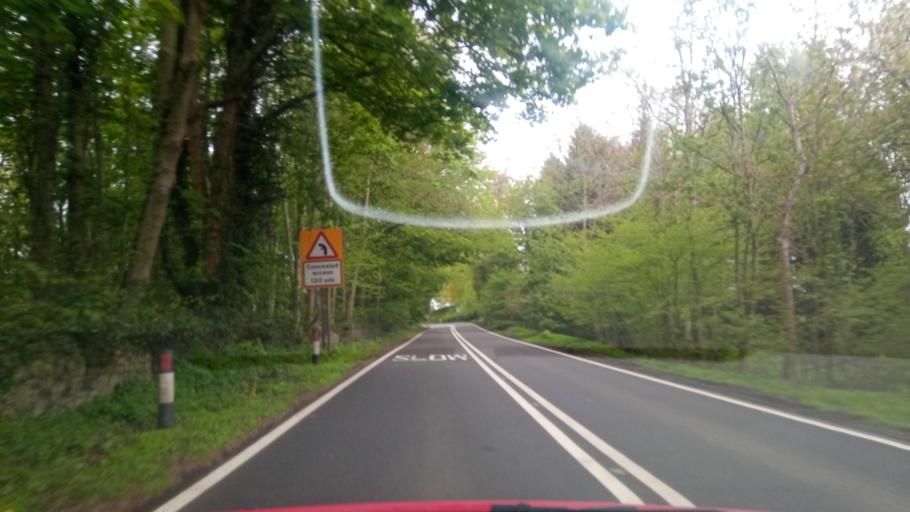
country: GB
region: Scotland
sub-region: The Scottish Borders
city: Jedburgh
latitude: 55.5156
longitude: -2.5808
